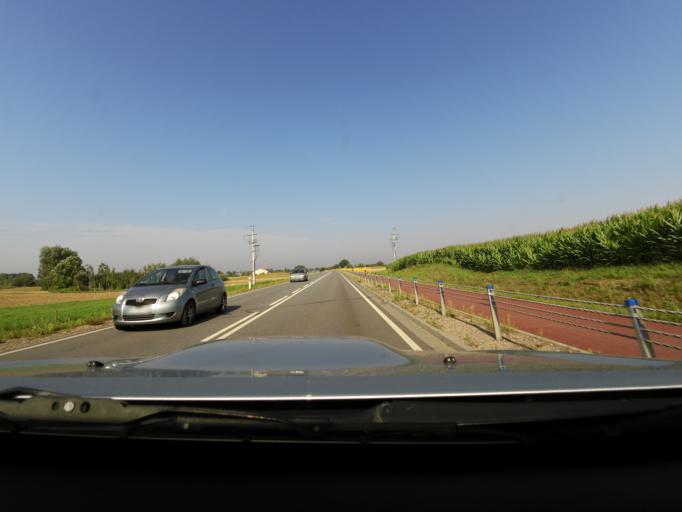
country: PL
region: Podlasie
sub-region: Powiat sejnenski
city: Krasnopol
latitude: 54.0985
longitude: 23.2072
